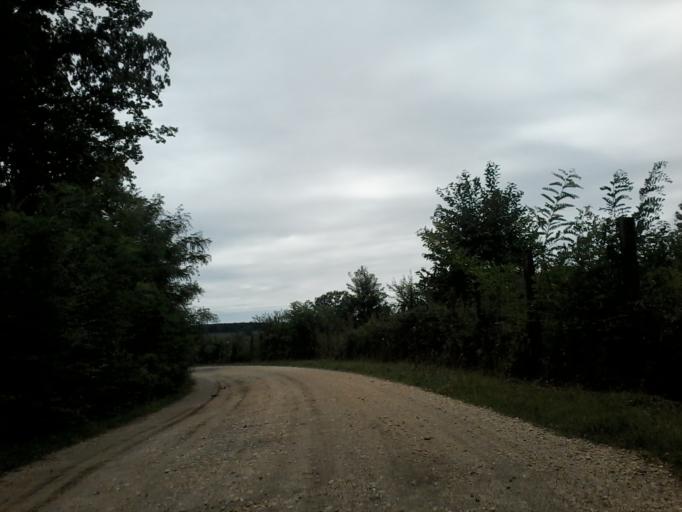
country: HU
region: Vas
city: Sarvar
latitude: 47.1598
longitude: 17.0236
